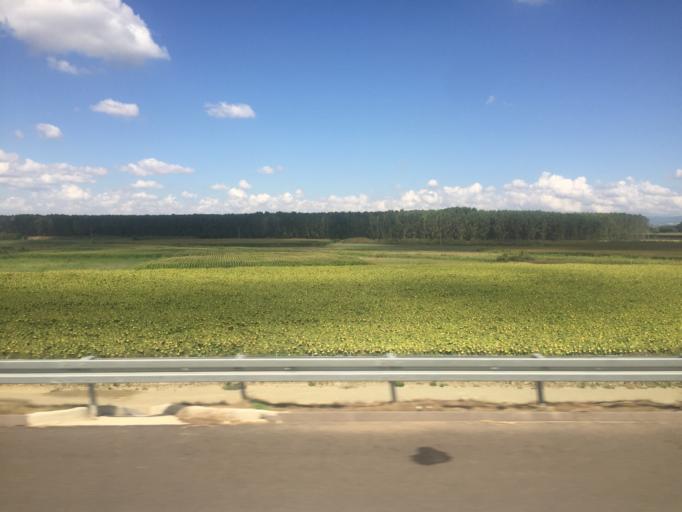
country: TR
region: Bursa
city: Karacabey
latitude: 40.1429
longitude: 28.3040
